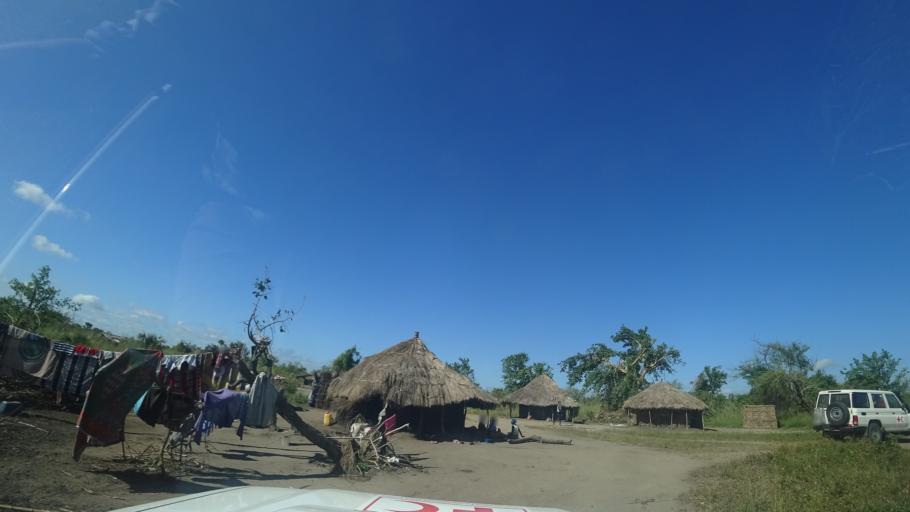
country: MZ
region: Sofala
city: Dondo
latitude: -19.4026
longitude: 34.5942
